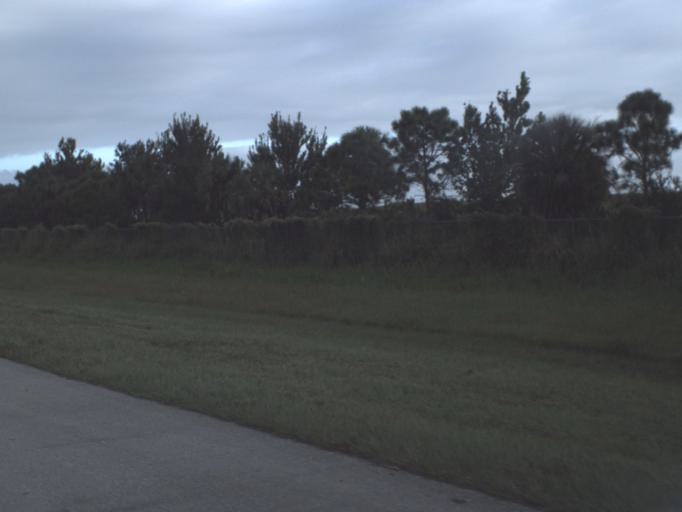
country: US
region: Florida
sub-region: Lee County
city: Bonita Springs
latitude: 26.3709
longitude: -81.7696
